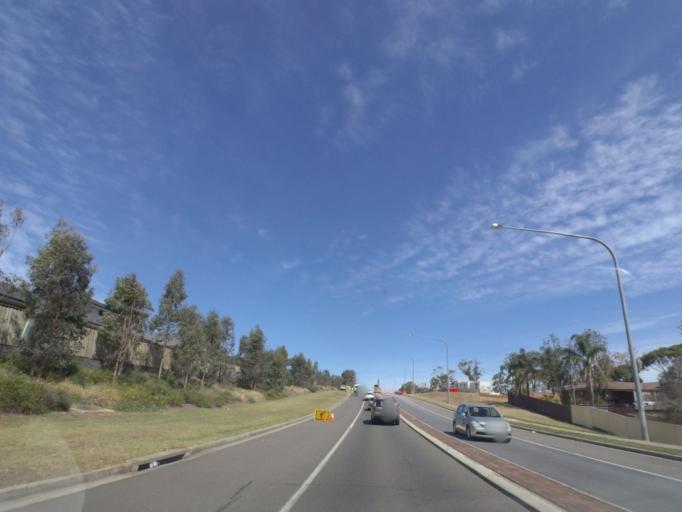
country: AU
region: New South Wales
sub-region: Campbelltown Municipality
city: Campbelltown
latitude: -34.0491
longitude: 150.8044
